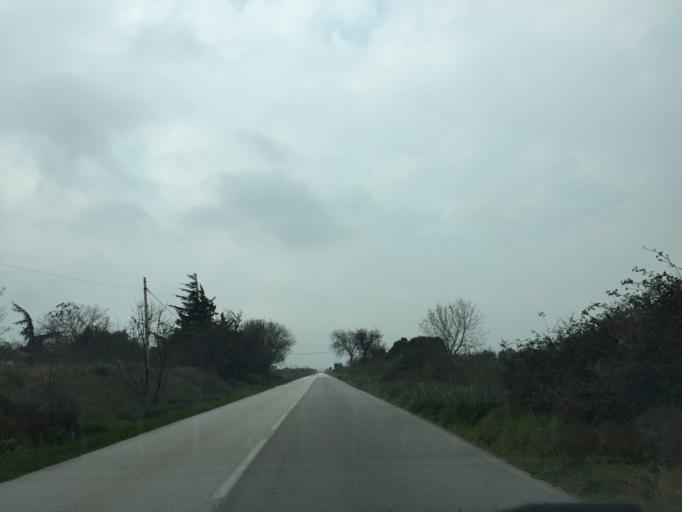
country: IT
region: Apulia
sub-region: Provincia di Foggia
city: Castelluccio dei Sauri
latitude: 41.4011
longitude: 15.4305
